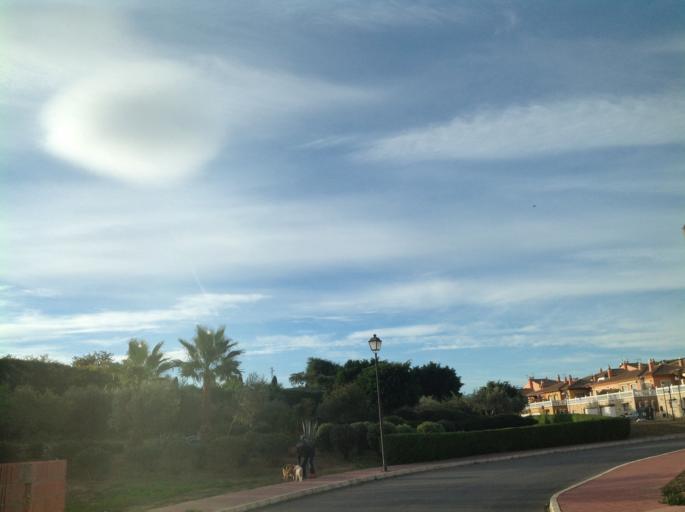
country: ES
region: Andalusia
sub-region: Provincia de Malaga
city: Pizarra
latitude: 36.7478
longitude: -4.7168
